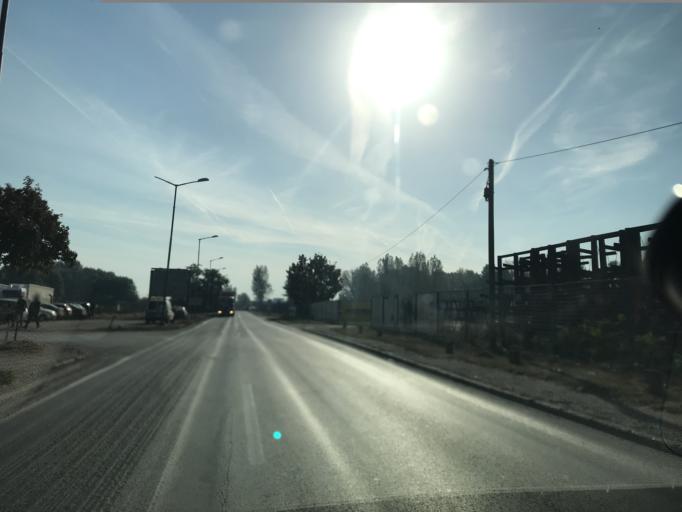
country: RS
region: Autonomna Pokrajina Vojvodina
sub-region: Juznobacki Okrug
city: Novi Sad
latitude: 45.2699
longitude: 19.8478
